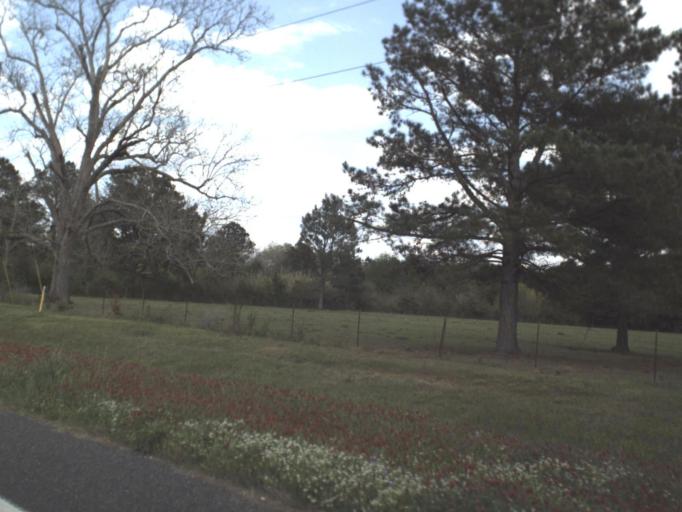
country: US
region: Florida
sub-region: Okaloosa County
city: Crestview
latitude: 30.8132
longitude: -86.5403
